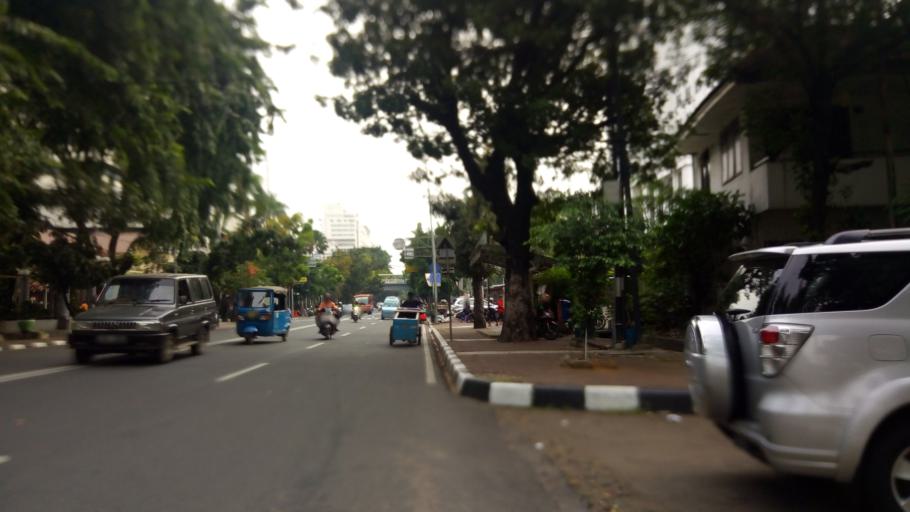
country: ID
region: Jakarta Raya
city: Jakarta
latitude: -6.1695
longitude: 106.8395
